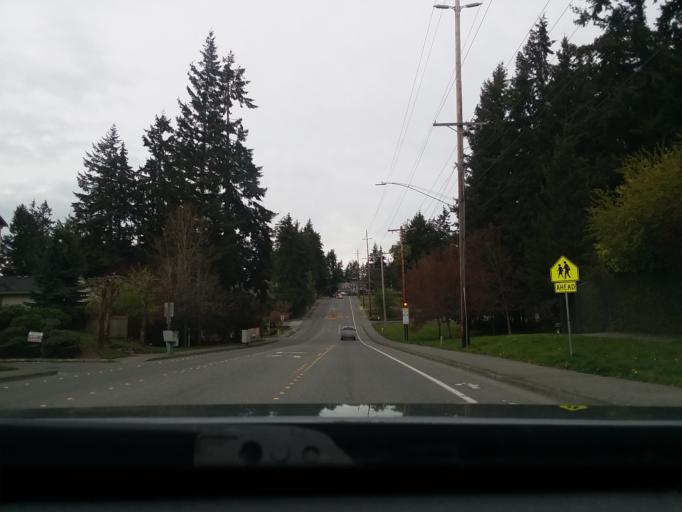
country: US
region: Washington
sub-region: Snohomish County
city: Lynnwood
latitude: 47.8106
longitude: -122.3311
